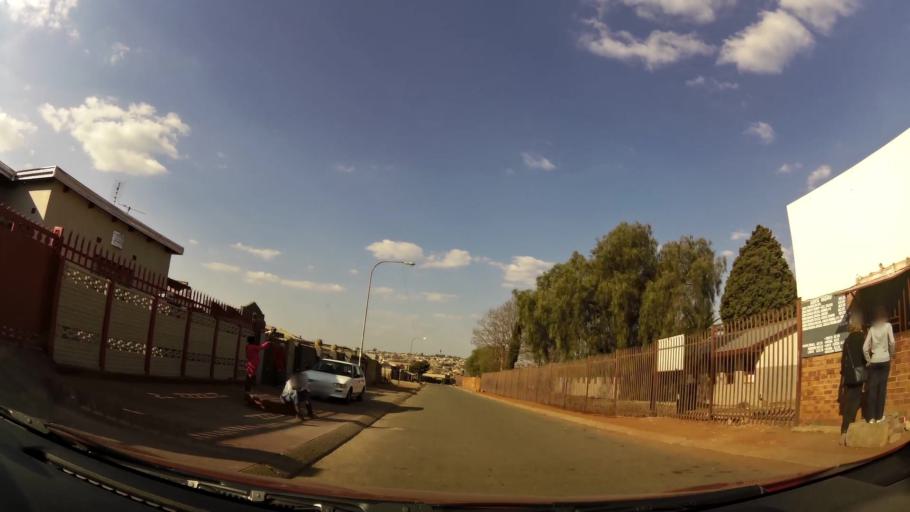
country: ZA
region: Gauteng
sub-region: City of Johannesburg Metropolitan Municipality
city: Soweto
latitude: -26.2175
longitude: 27.8731
